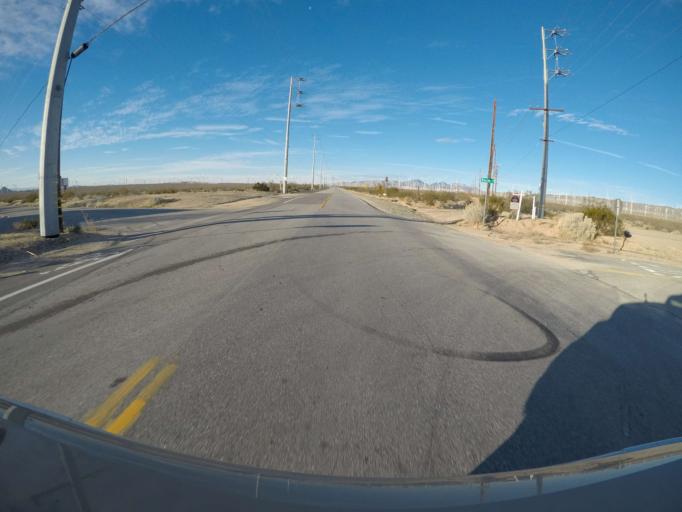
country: US
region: California
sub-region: Kern County
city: Mojave
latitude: 35.0537
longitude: -118.1944
